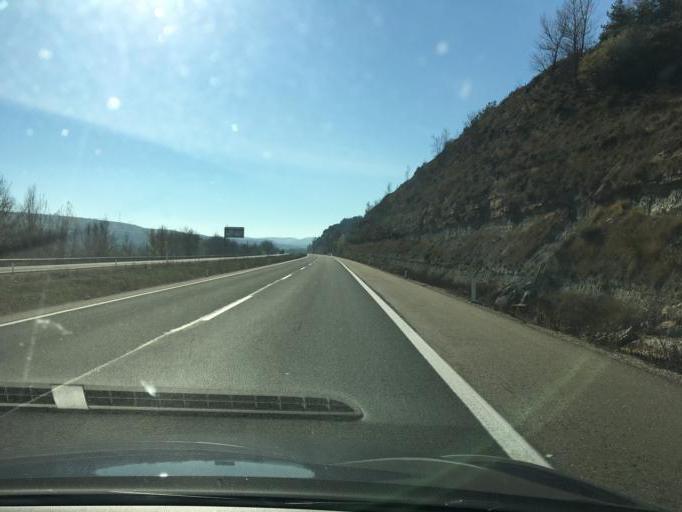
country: ES
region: Castille and Leon
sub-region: Provincia de Burgos
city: Pradanos de Bureba
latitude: 42.5184
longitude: -3.3418
